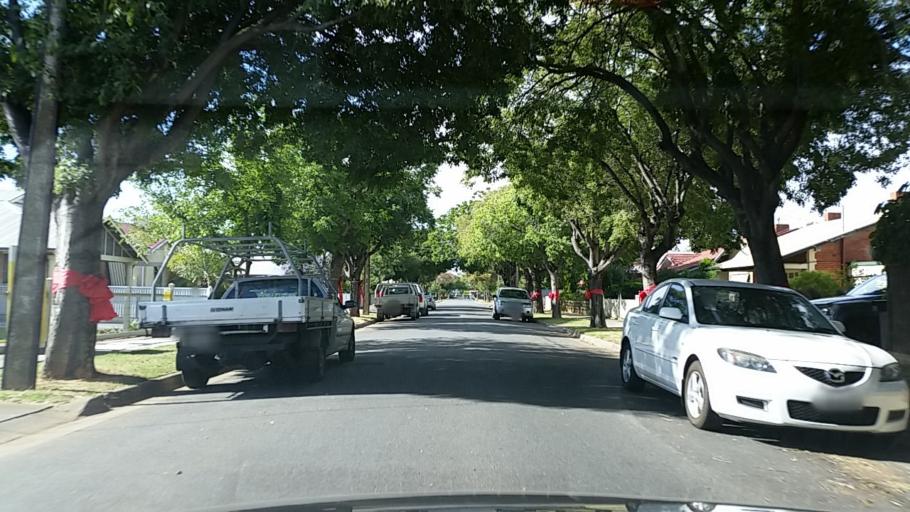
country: AU
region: South Australia
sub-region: Charles Sturt
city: Allenby Gardens
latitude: -34.8995
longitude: 138.5529
